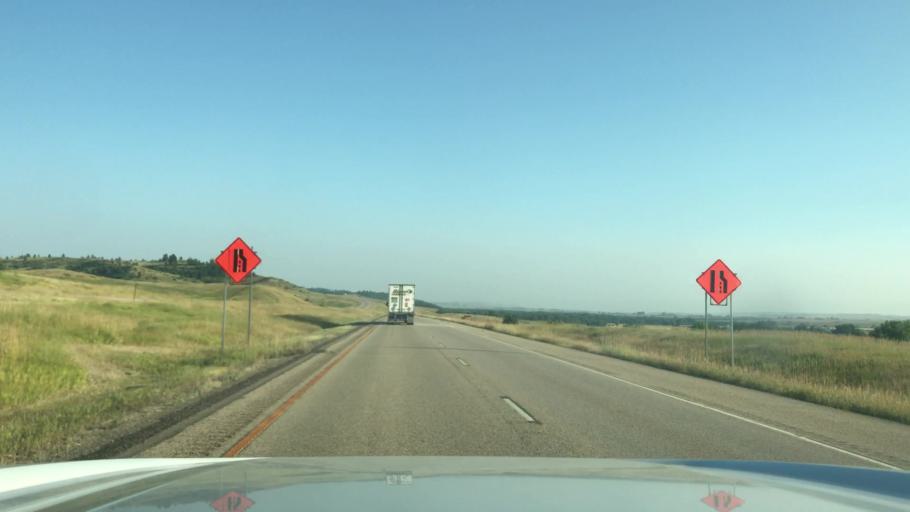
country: US
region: Montana
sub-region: Big Horn County
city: Crow Agency
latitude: 45.3863
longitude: -107.3706
